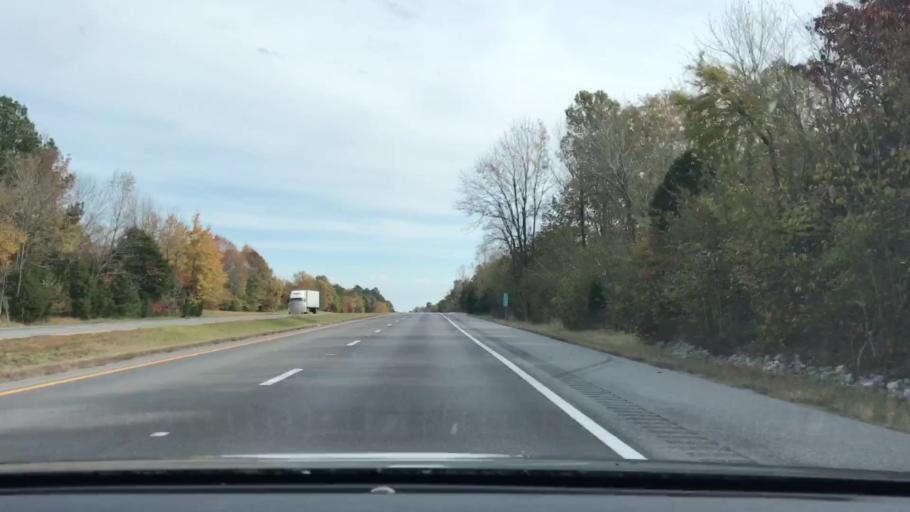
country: US
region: Kentucky
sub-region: Marshall County
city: Benton
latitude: 36.8370
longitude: -88.4278
